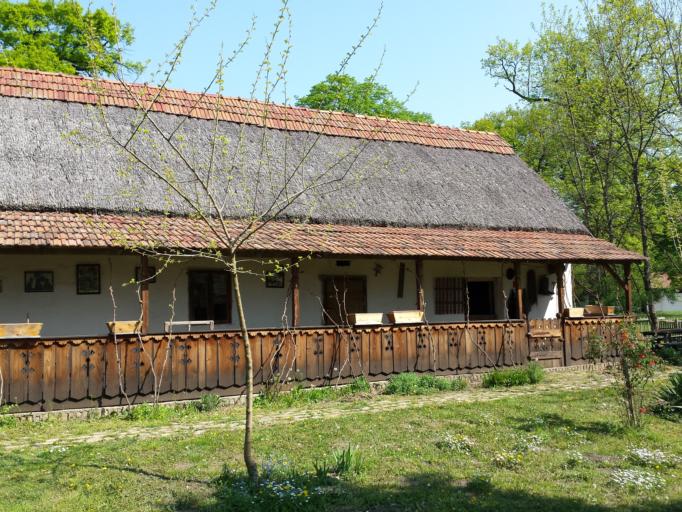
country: RO
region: Timis
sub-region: Comuna Dumbravita
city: Dumbravita
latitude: 45.7789
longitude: 21.2635
